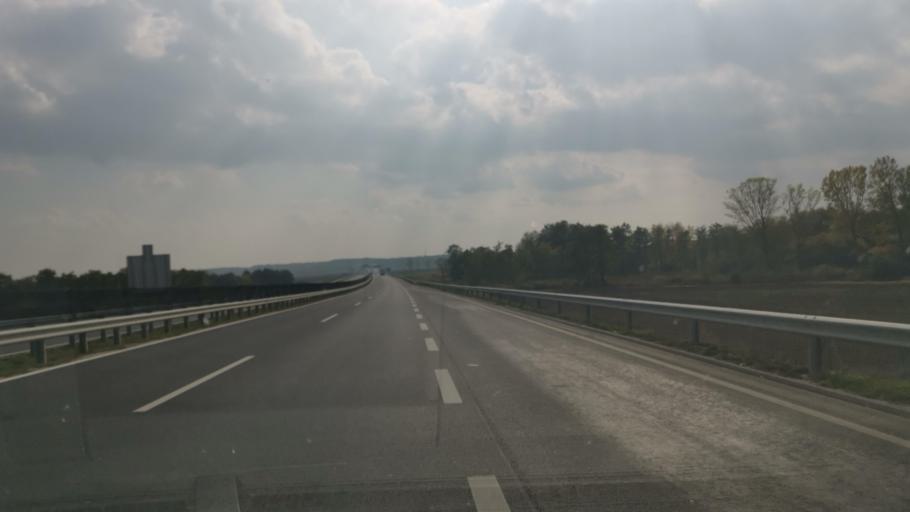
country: HU
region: Gyor-Moson-Sopron
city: Sopron
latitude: 47.6511
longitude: 16.6263
